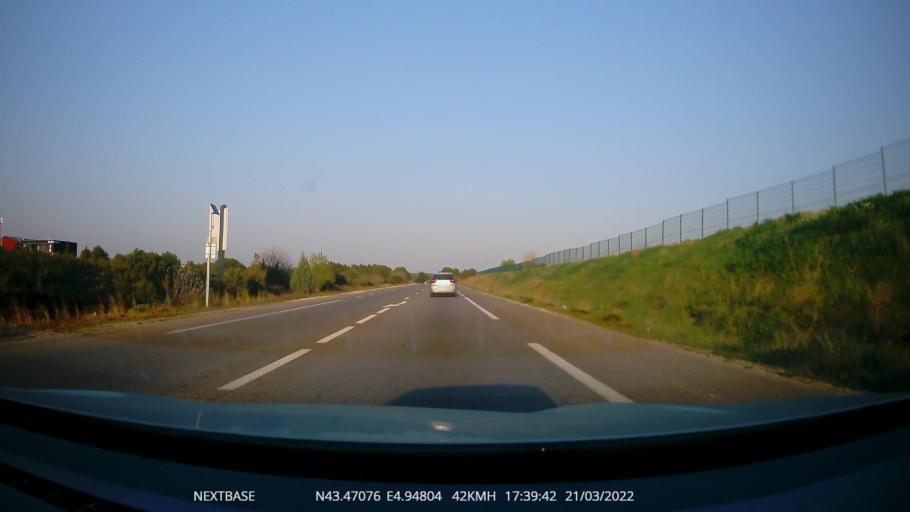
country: FR
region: Provence-Alpes-Cote d'Azur
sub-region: Departement des Bouches-du-Rhone
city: Fos-sur-Mer
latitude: 43.4708
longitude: 4.9482
